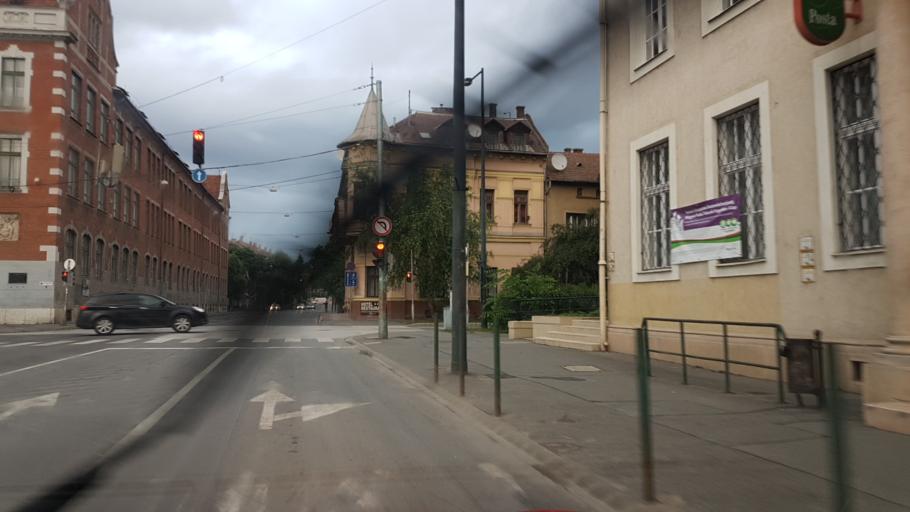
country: HU
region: Borsod-Abauj-Zemplen
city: Miskolc
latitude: 48.1050
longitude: 20.7855
